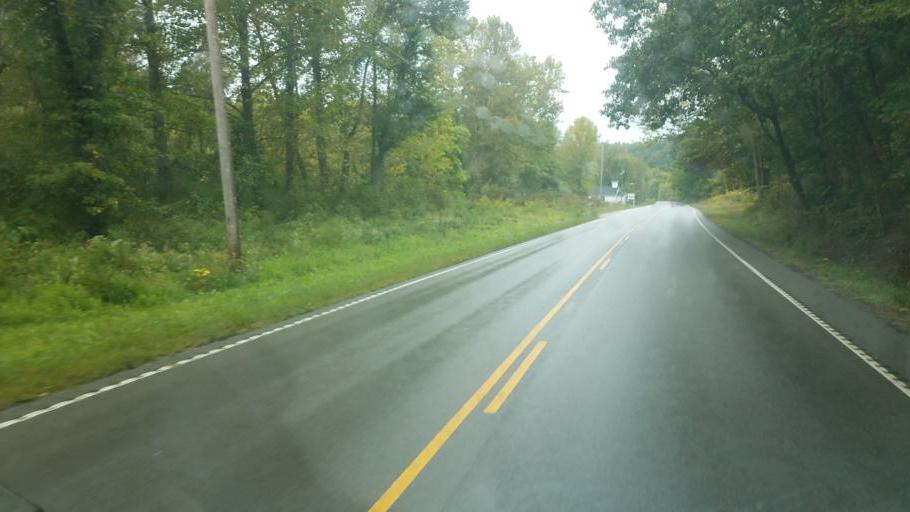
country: US
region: Ohio
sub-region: Jackson County
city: Oak Hill
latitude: 38.8323
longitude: -82.6559
